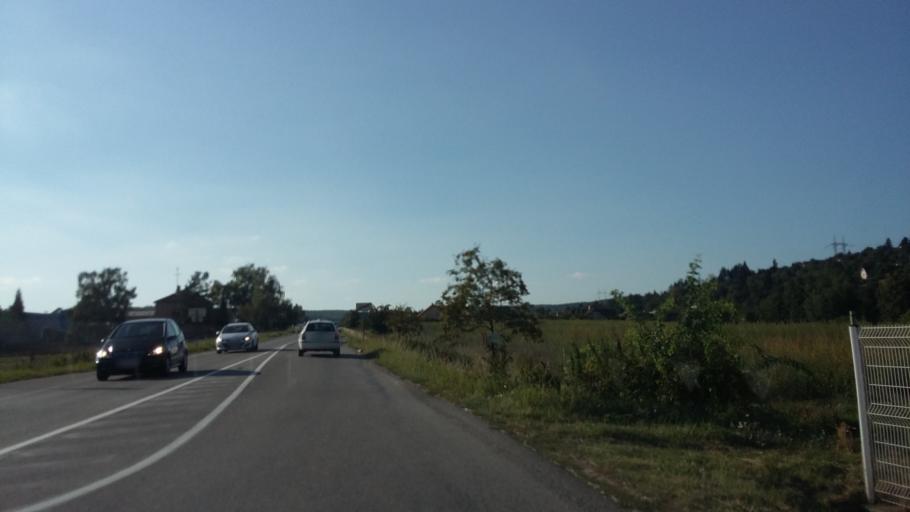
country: CZ
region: South Moravian
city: Troubsko
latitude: 49.1780
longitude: 16.4986
